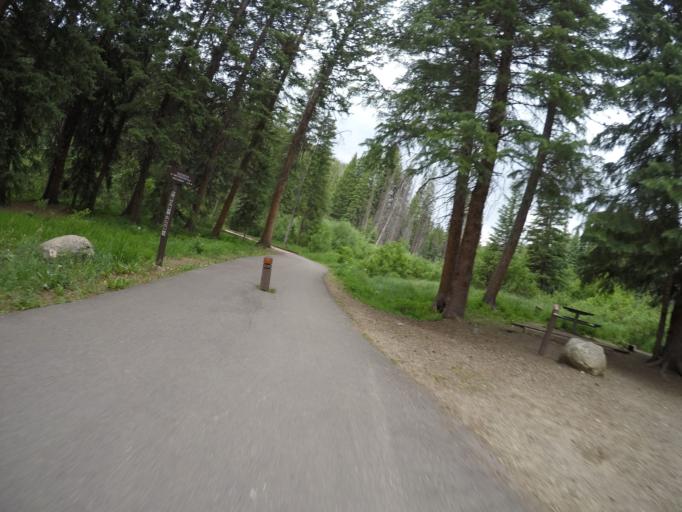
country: US
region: Colorado
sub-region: Grand County
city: Fraser
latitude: 39.9034
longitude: -105.7781
